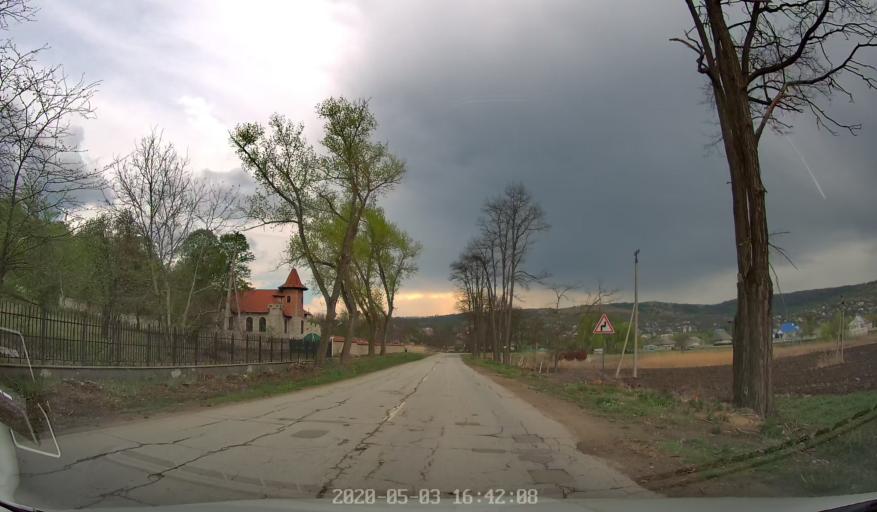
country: MD
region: Stinga Nistrului
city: Bucovat
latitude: 47.1614
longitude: 28.4173
